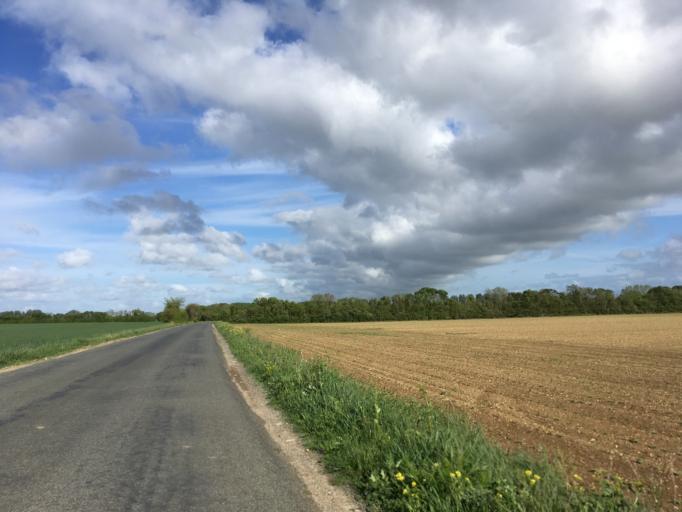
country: FR
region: Poitou-Charentes
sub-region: Departement de la Charente-Maritime
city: Verines
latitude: 46.1786
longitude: -0.9362
